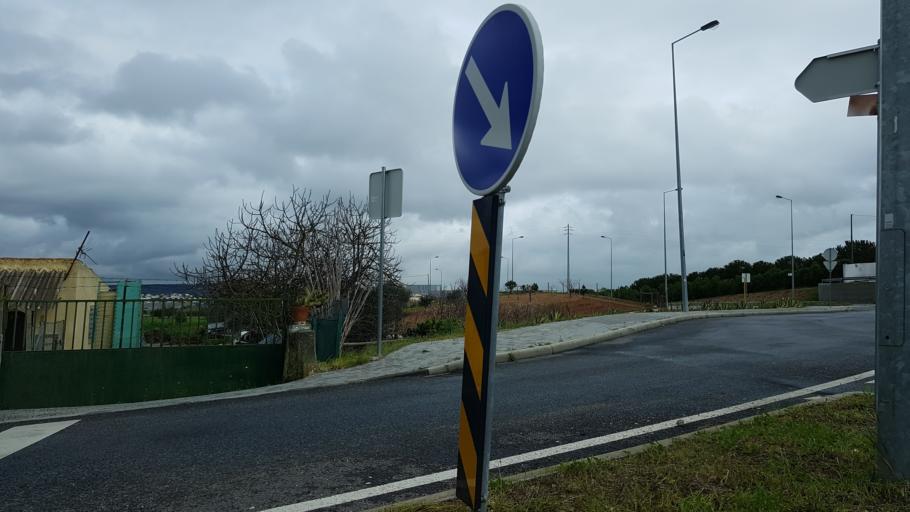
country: PT
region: Lisbon
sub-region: Alenquer
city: Alenquer
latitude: 39.0353
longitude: -8.9963
